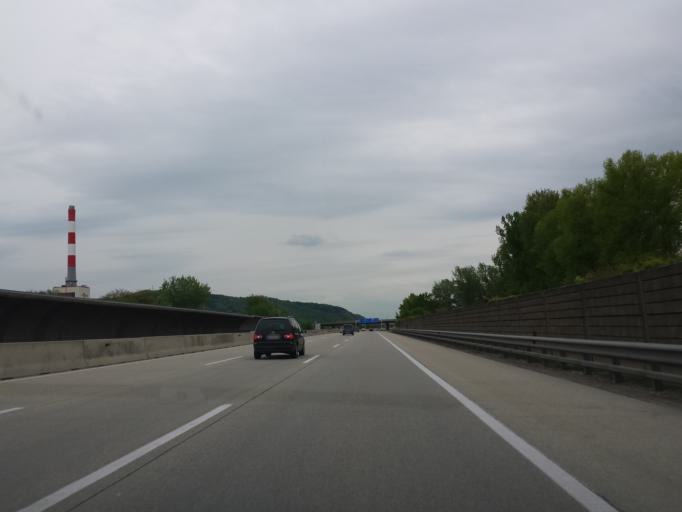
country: AT
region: Lower Austria
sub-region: Politischer Bezirk Korneuburg
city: Korneuburg
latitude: 48.3348
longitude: 16.3301
